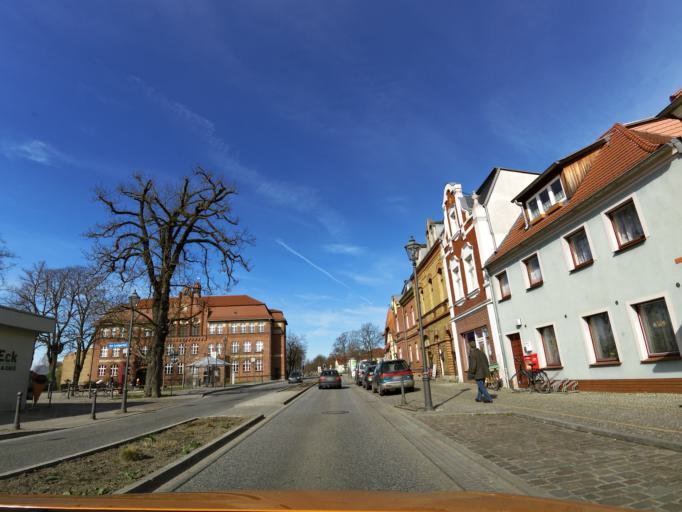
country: DE
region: Brandenburg
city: Beelitz
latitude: 52.2354
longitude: 12.9781
